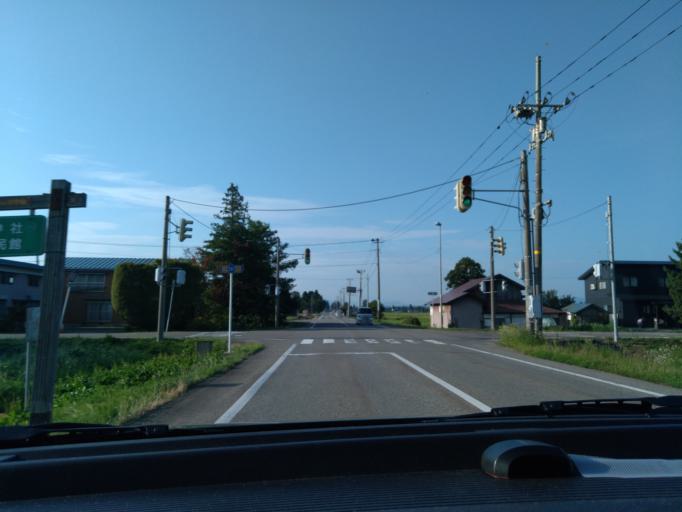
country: JP
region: Akita
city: Kakunodatemachi
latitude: 39.5198
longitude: 140.5584
